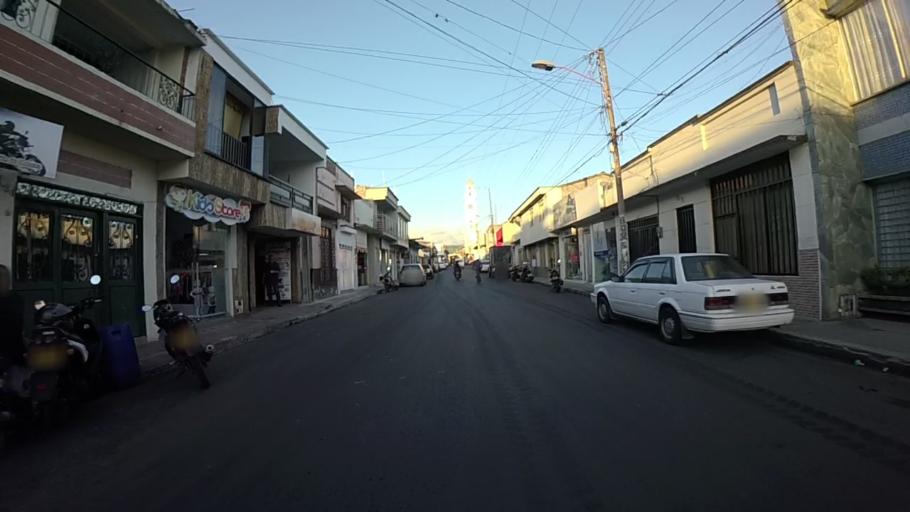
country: CO
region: Valle del Cauca
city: Cartago
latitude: 4.7493
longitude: -75.9182
